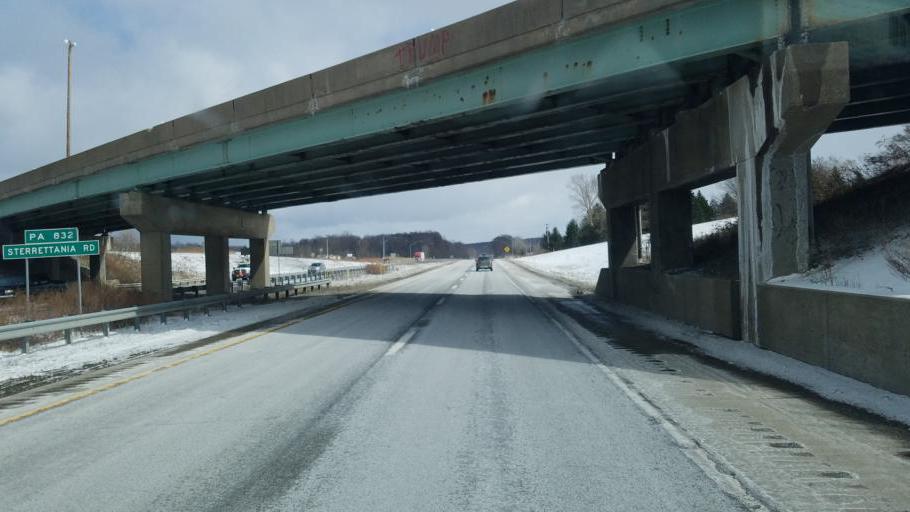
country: US
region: Pennsylvania
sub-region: Erie County
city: Fairview
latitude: 42.0183
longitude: -80.1888
